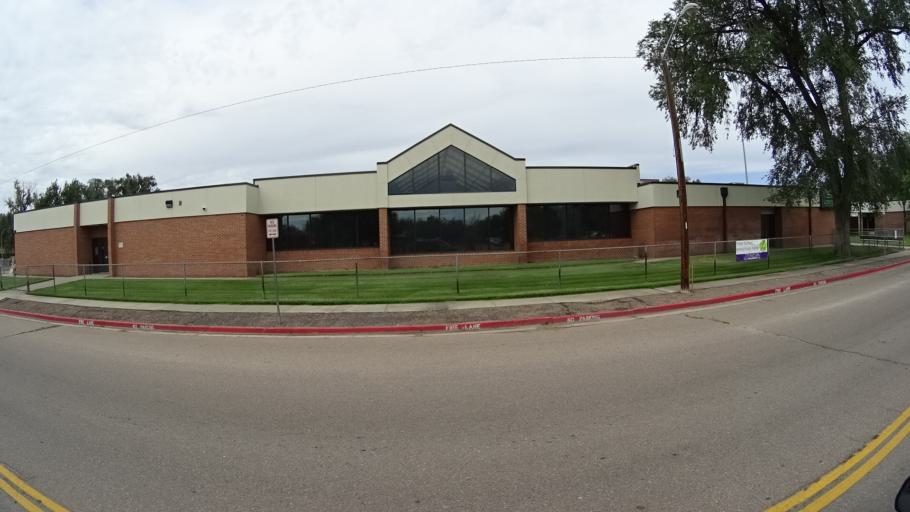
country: US
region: Colorado
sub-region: El Paso County
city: Fountain
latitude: 38.6816
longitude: -104.7006
